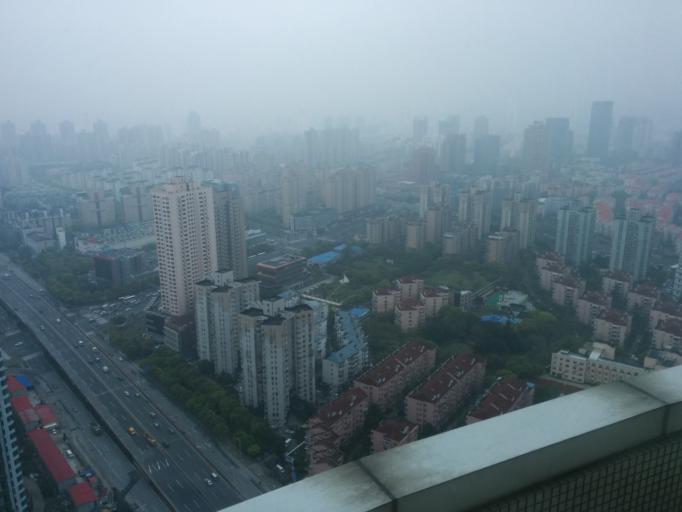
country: CN
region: Shanghai Shi
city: Huamu
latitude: 31.2133
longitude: 121.5300
